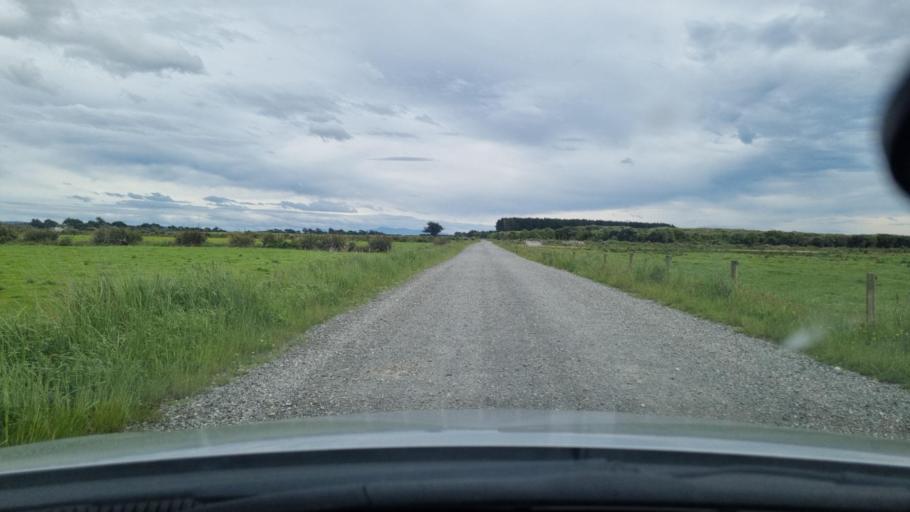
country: NZ
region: Southland
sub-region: Invercargill City
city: Invercargill
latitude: -46.4027
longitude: 168.2817
